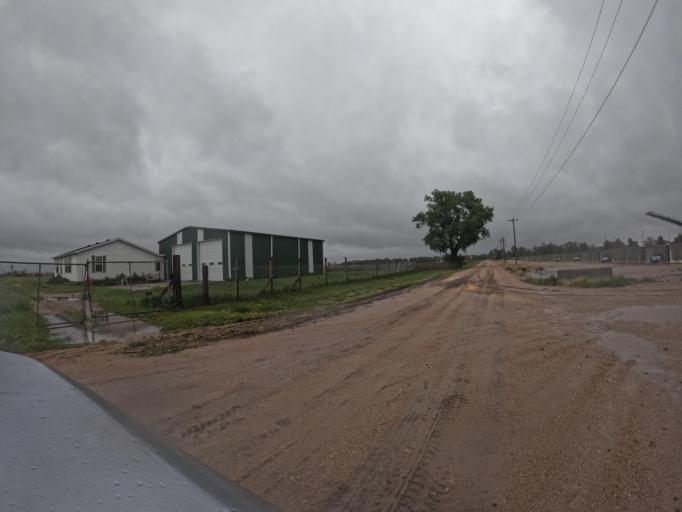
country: US
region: Nebraska
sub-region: Clay County
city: Harvard
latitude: 40.6118
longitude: -98.1027
